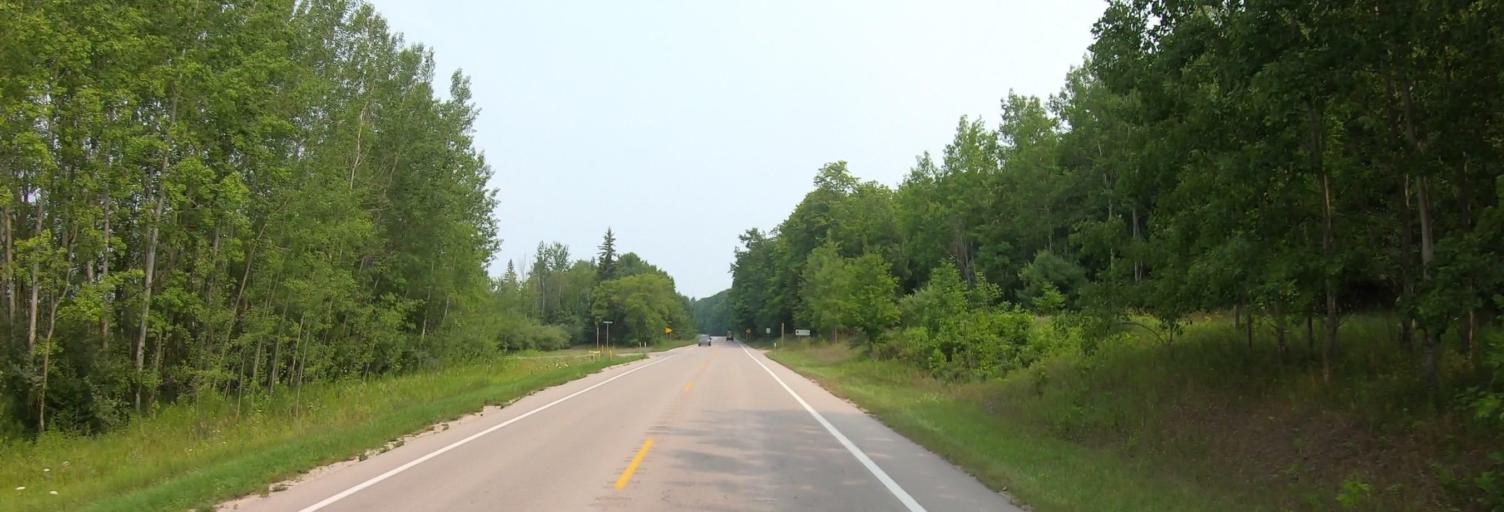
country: US
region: Michigan
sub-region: Leelanau County
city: Leland
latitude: 44.9273
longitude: -85.8180
